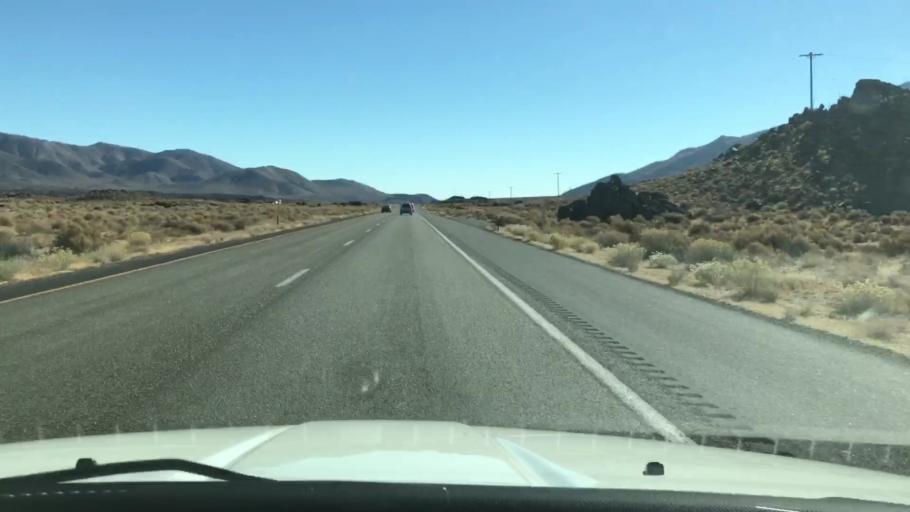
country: US
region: California
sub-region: Kern County
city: Inyokern
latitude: 35.9760
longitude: -117.9234
